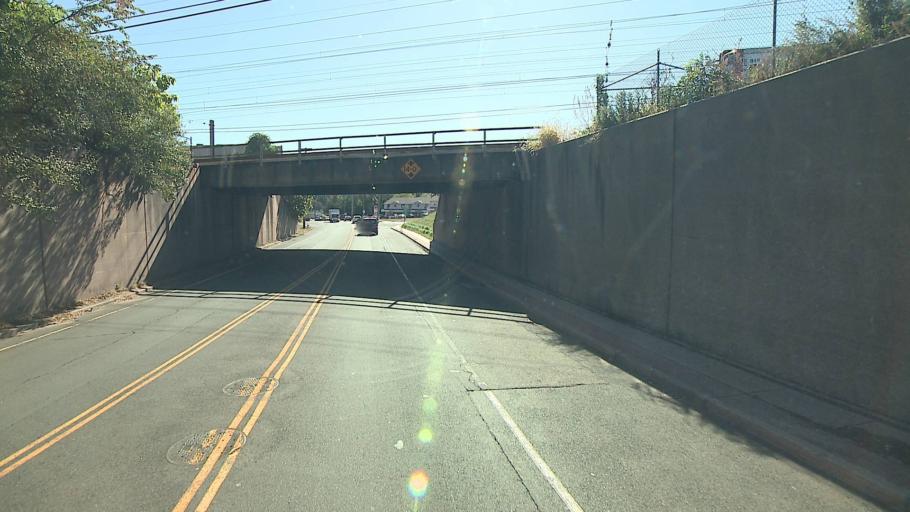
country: US
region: Connecticut
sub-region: New Haven County
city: West Haven
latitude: 41.2720
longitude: -72.9612
